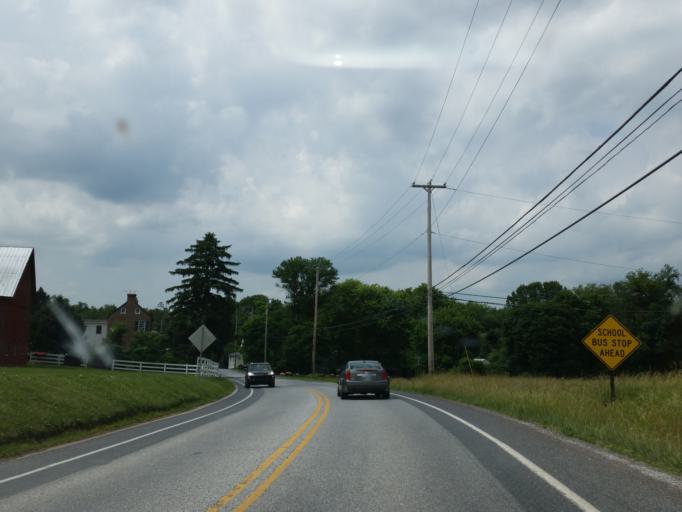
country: US
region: Delaware
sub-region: New Castle County
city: Newark
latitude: 39.7324
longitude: -75.7917
